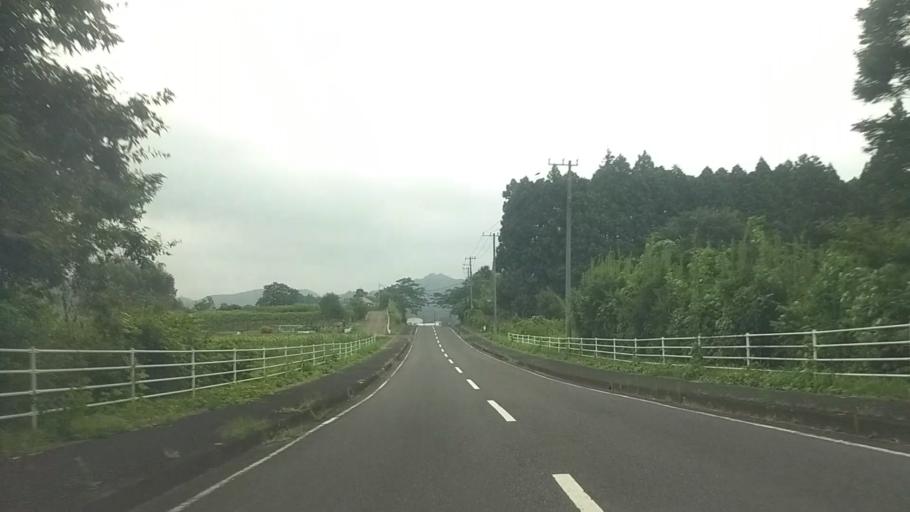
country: JP
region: Chiba
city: Kawaguchi
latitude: 35.2353
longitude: 140.0854
